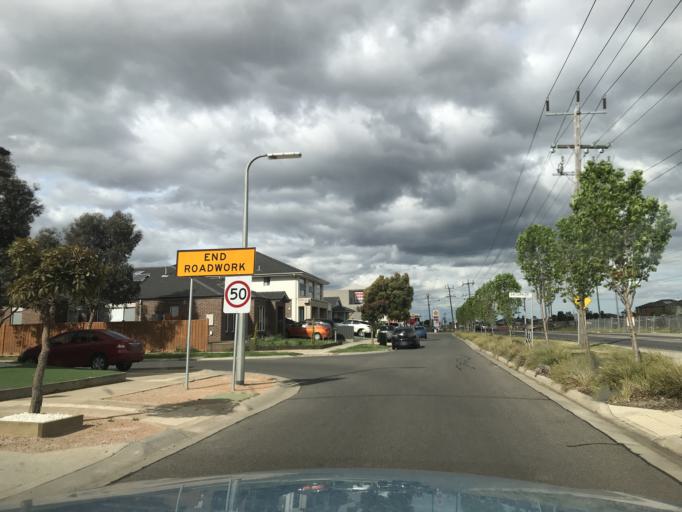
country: AU
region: Victoria
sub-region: Wyndham
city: Williams Landing
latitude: -37.8536
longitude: 144.7433
